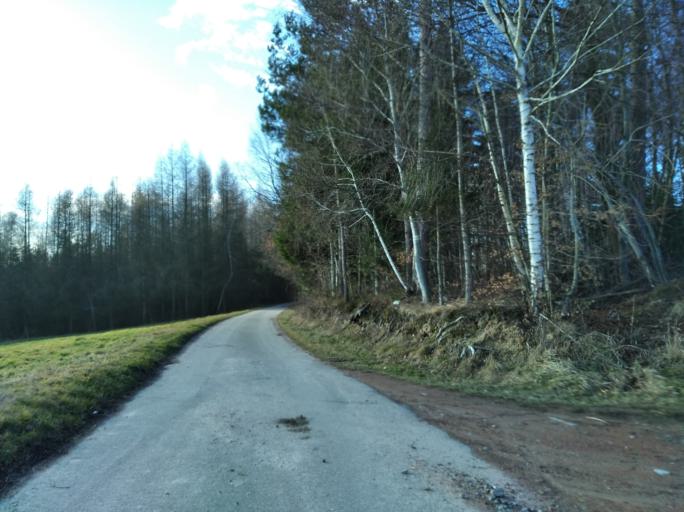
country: PL
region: Subcarpathian Voivodeship
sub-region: Powiat strzyzowski
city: Wisniowa
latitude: 49.9013
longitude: 21.7103
